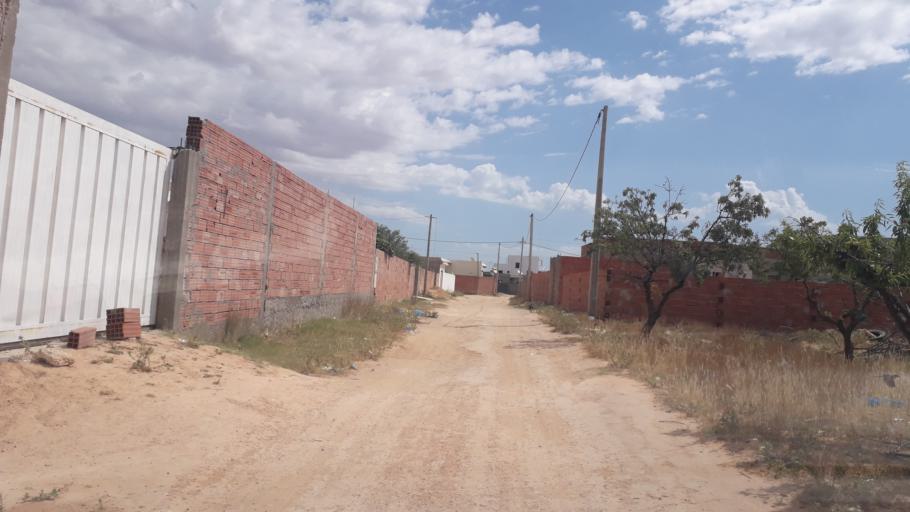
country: TN
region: Safaqis
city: Al Qarmadah
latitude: 34.8379
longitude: 10.7736
